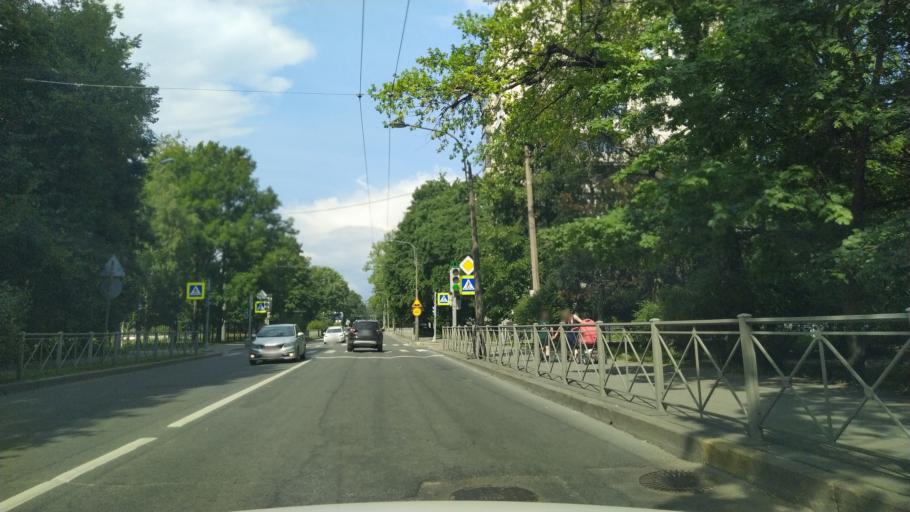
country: RU
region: Leningrad
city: Sampsonievskiy
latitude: 59.9982
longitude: 30.3466
